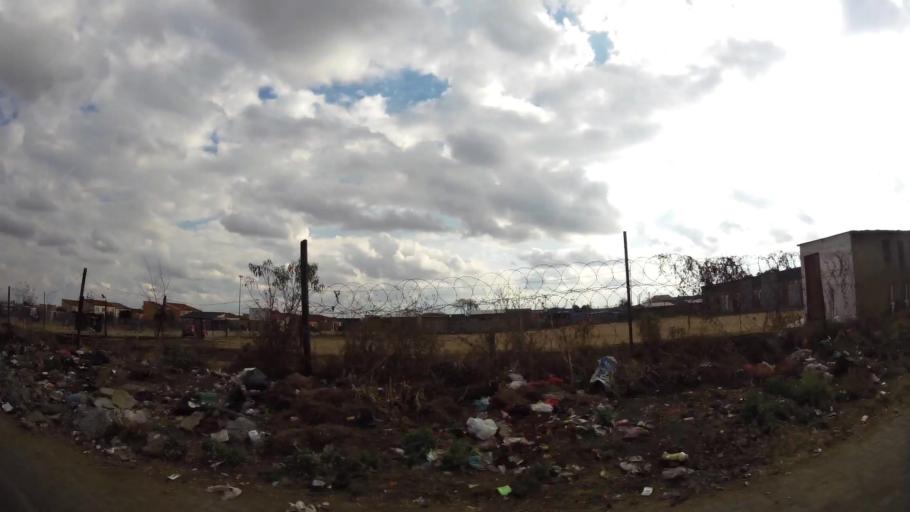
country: ZA
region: Orange Free State
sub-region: Fezile Dabi District Municipality
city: Sasolburg
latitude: -26.8421
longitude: 27.8437
